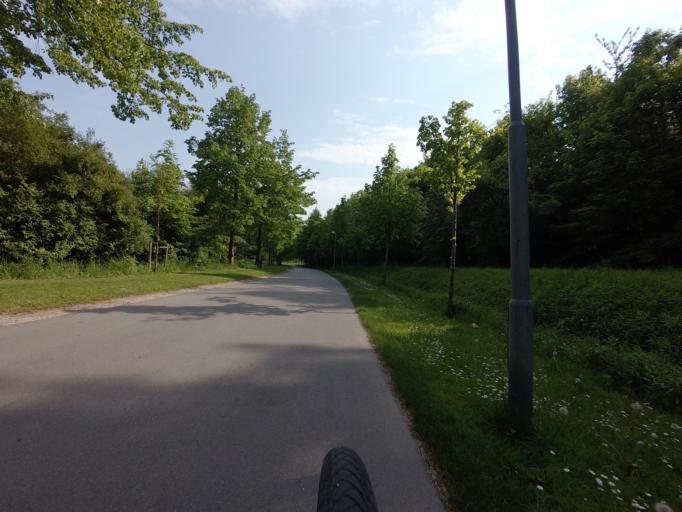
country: DK
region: Capital Region
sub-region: Brondby Kommune
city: Brondbyvester
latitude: 55.6515
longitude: 12.4262
